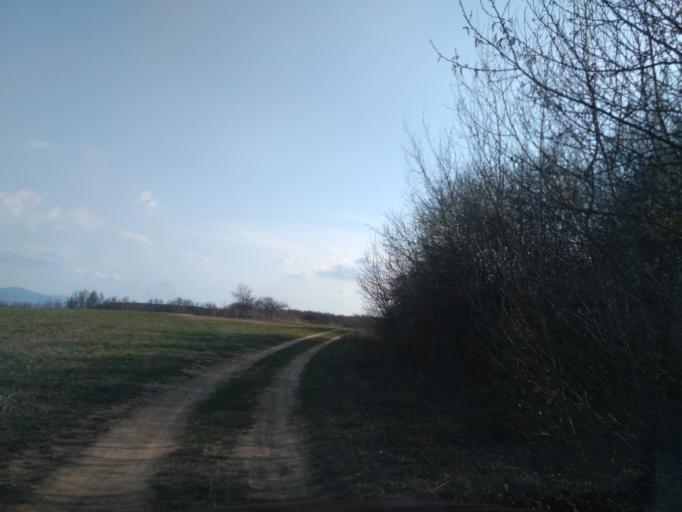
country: SK
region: Kosicky
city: Kosice
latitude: 48.6794
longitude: 21.1813
